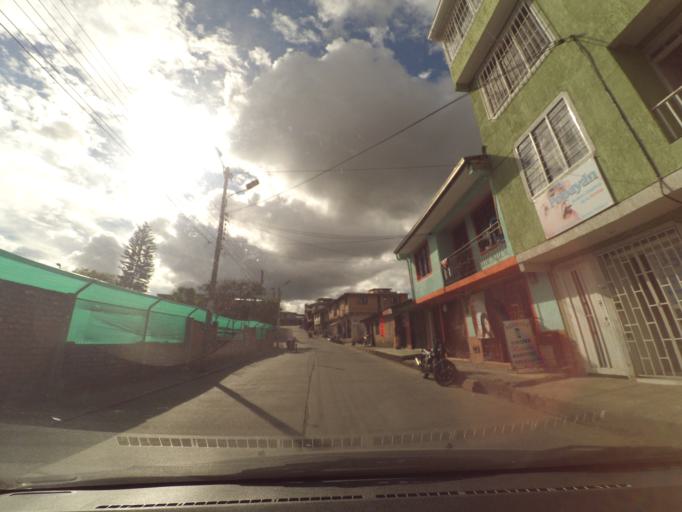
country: CO
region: Cauca
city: Popayan
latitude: 2.4444
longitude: -76.6272
